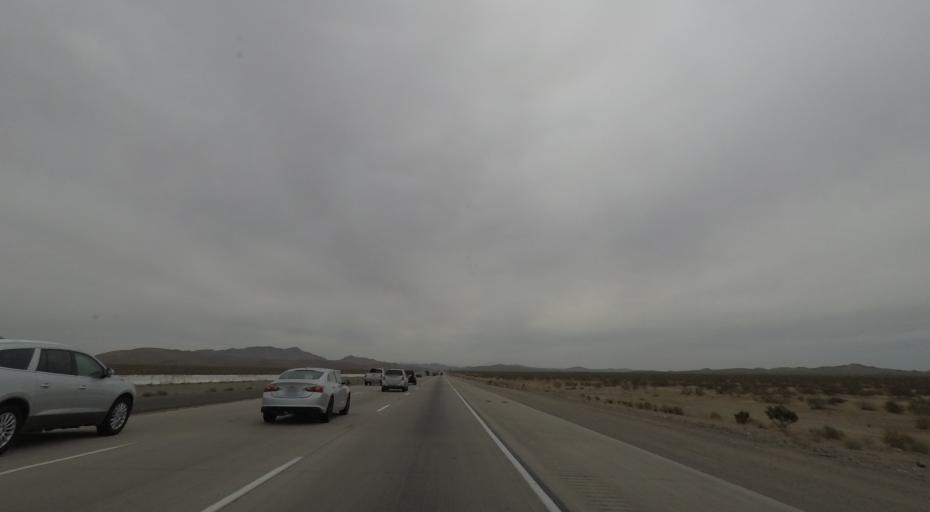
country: US
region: California
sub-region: San Bernardino County
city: Lenwood
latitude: 34.7938
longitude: -117.1165
